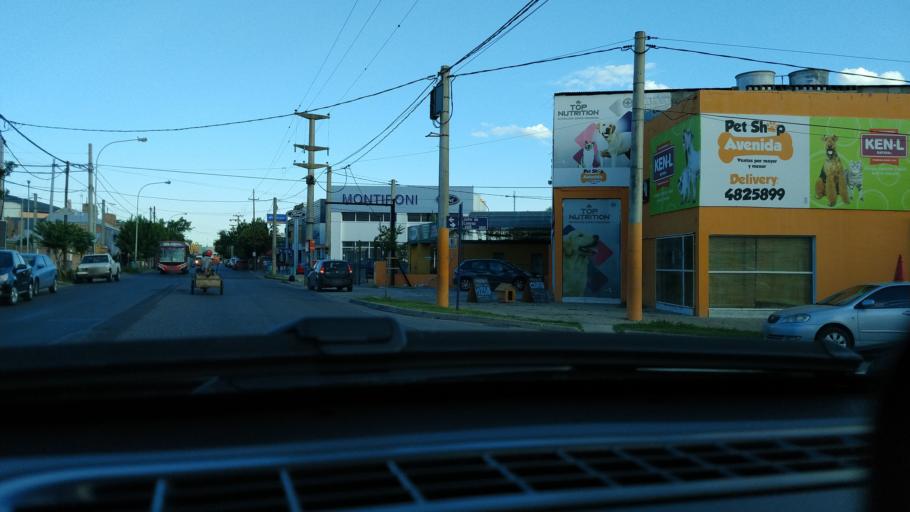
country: AR
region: Cordoba
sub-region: Departamento de Capital
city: Cordoba
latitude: -31.3644
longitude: -64.2245
